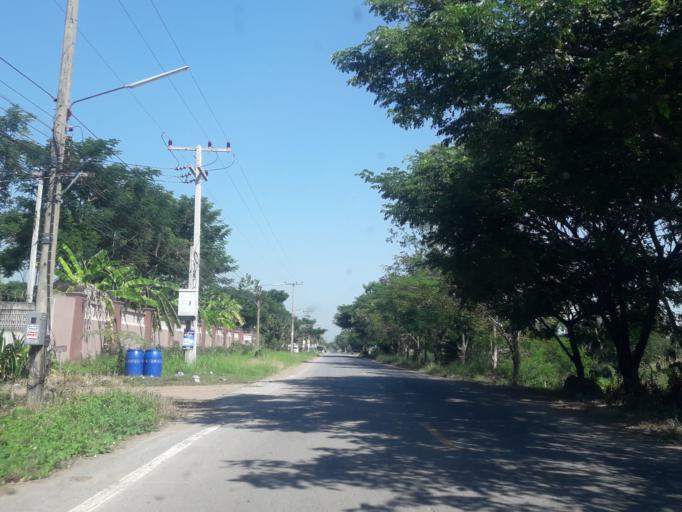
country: TH
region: Pathum Thani
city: Nong Suea
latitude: 14.1165
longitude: 100.8685
